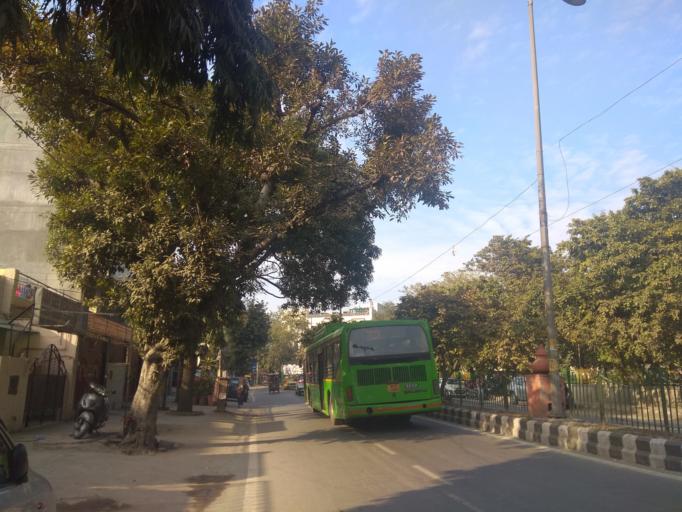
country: IN
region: NCT
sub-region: West Delhi
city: Nangloi Jat
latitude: 28.6293
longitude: 77.0688
